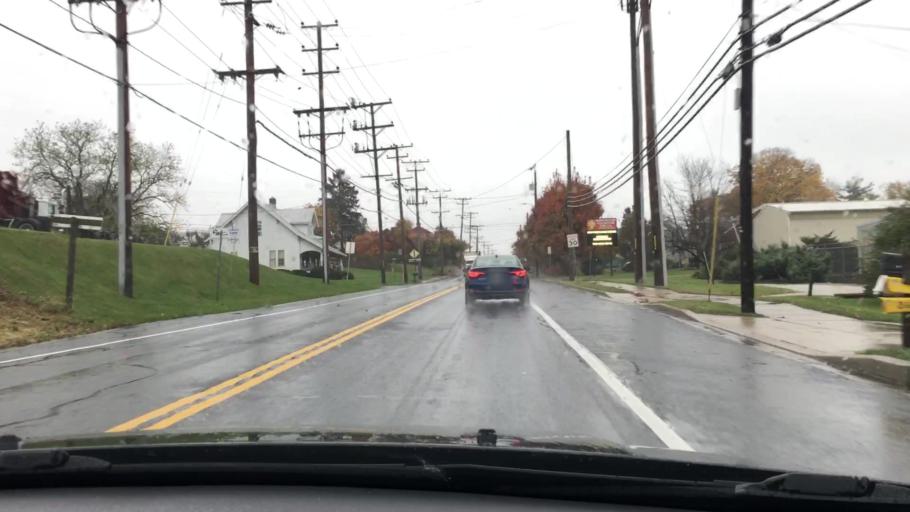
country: US
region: Maryland
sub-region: Carroll County
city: Manchester
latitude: 39.6669
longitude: -76.8886
